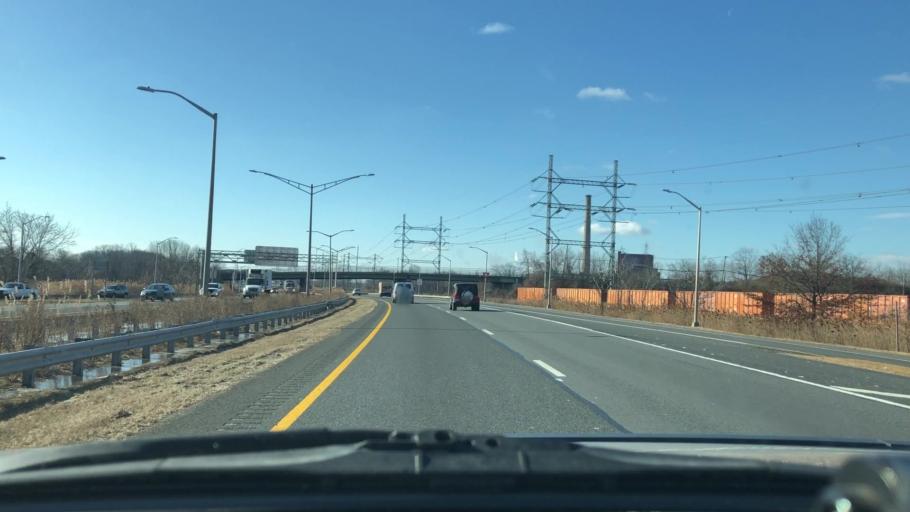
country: US
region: New York
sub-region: Richmond County
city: Bloomfield
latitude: 40.5999
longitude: -74.1901
